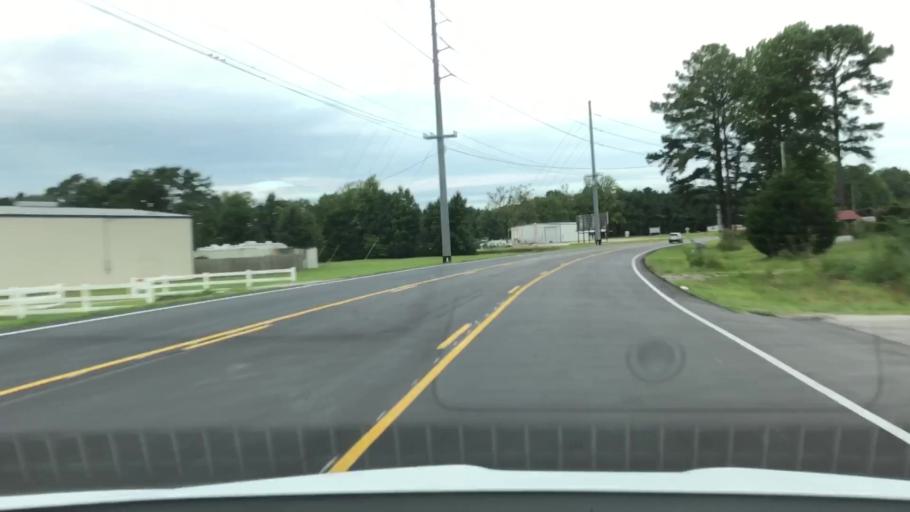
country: US
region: North Carolina
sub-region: Onslow County
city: Swansboro
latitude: 34.7914
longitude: -77.1308
